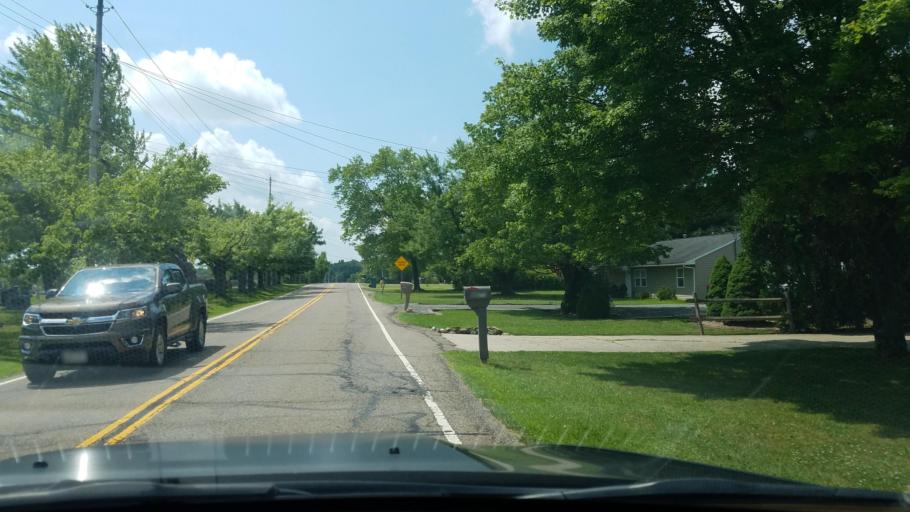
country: US
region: Ohio
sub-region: Trumbull County
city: Champion Heights
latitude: 41.2873
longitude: -80.8642
